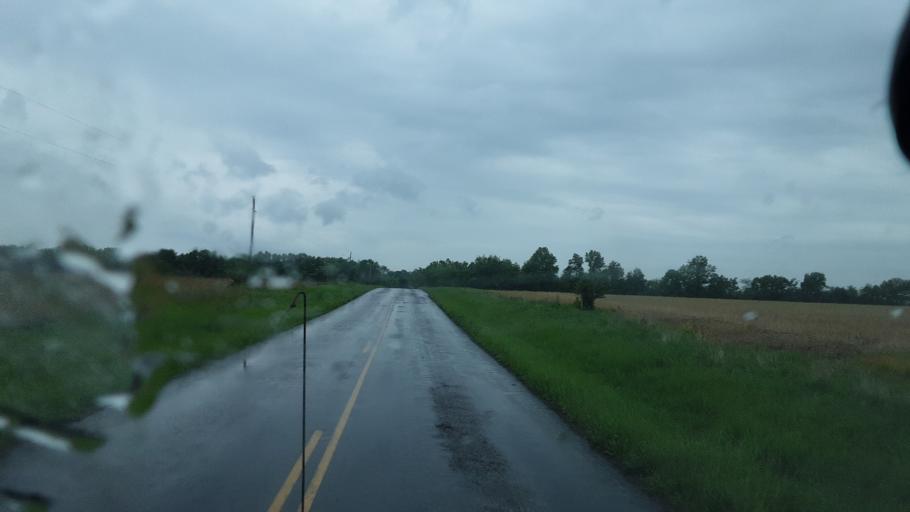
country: US
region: Missouri
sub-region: Randolph County
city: Moberly
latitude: 39.3899
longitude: -92.2483
